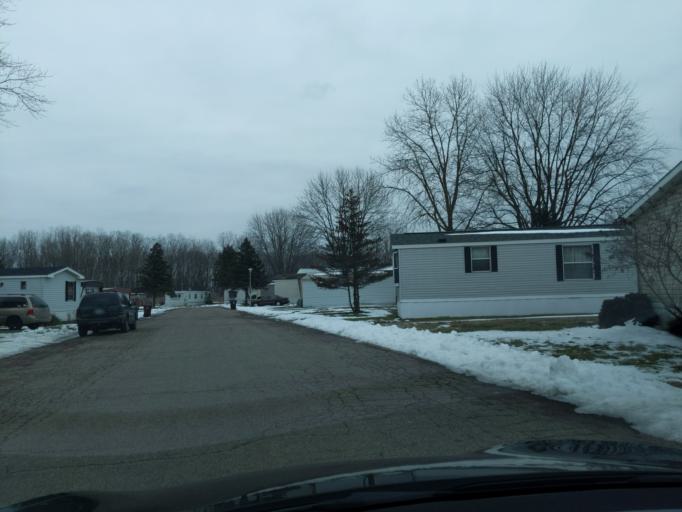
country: US
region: Michigan
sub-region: Ingham County
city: Lansing
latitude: 42.7739
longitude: -84.5518
